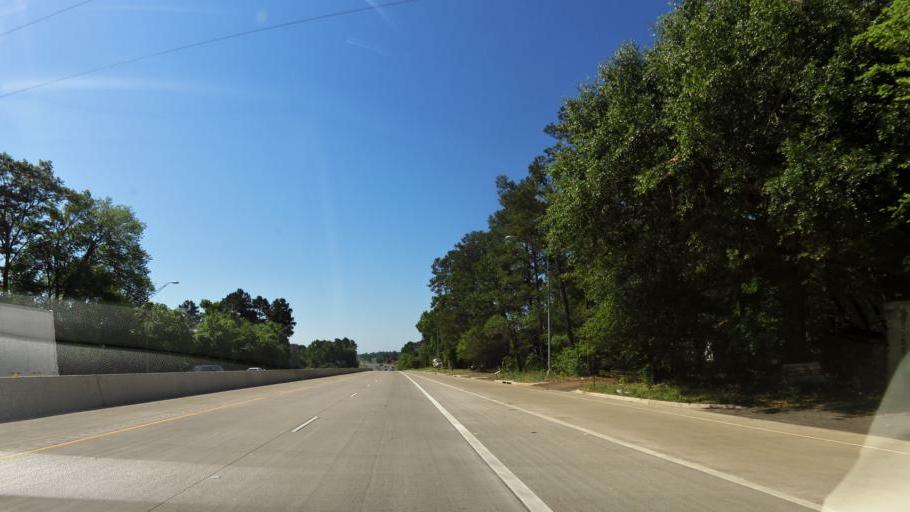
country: US
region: Texas
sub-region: Angelina County
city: Redland
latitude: 31.4034
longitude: -94.7198
